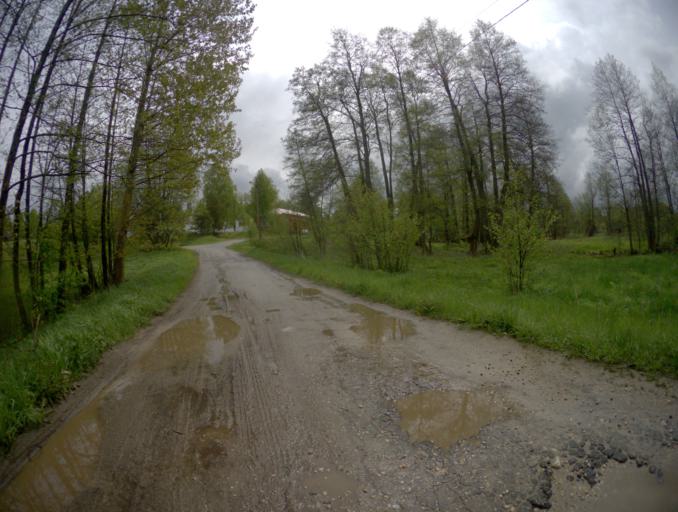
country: RU
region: Vladimir
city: Velikodvorskiy
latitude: 55.3707
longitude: 40.8596
